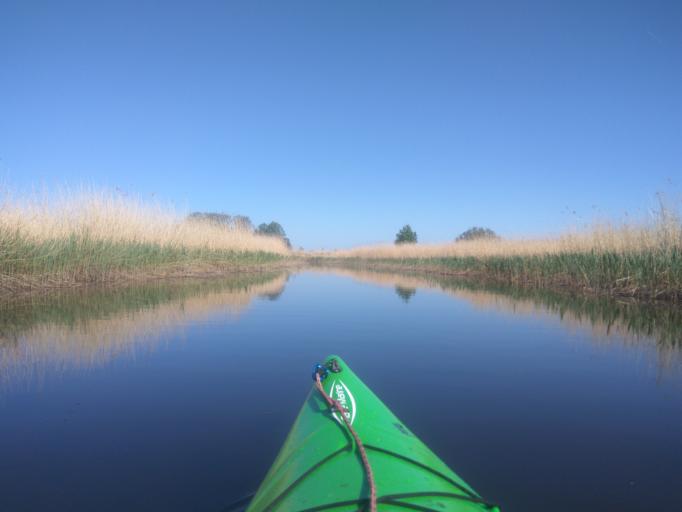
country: LV
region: Liepaja
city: Liepaja
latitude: 56.5190
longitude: 21.0627
